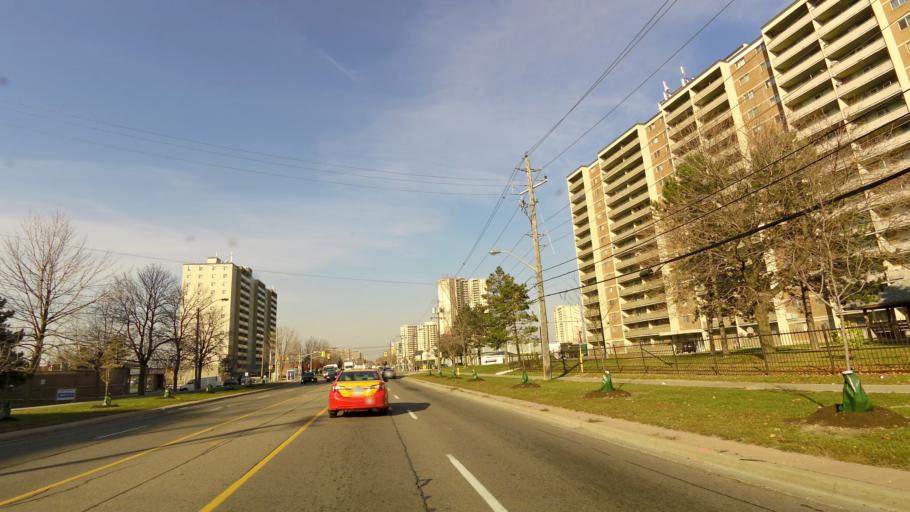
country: CA
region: Ontario
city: Concord
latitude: 43.7537
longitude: -79.5167
